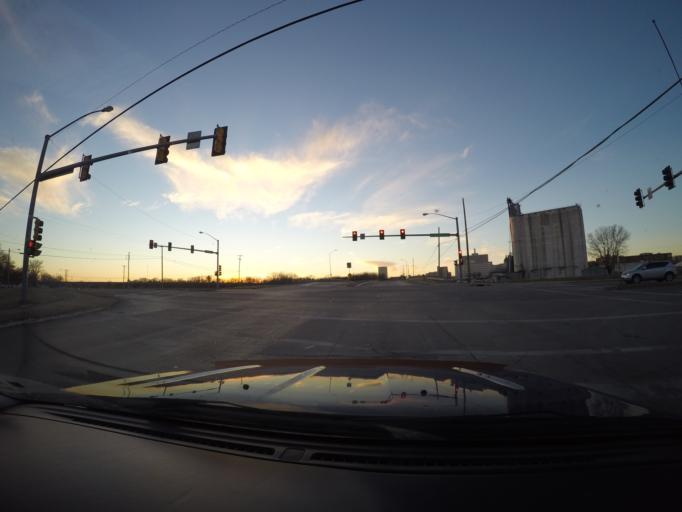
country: US
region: Kansas
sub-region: Shawnee County
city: Topeka
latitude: 39.0443
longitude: -95.6651
